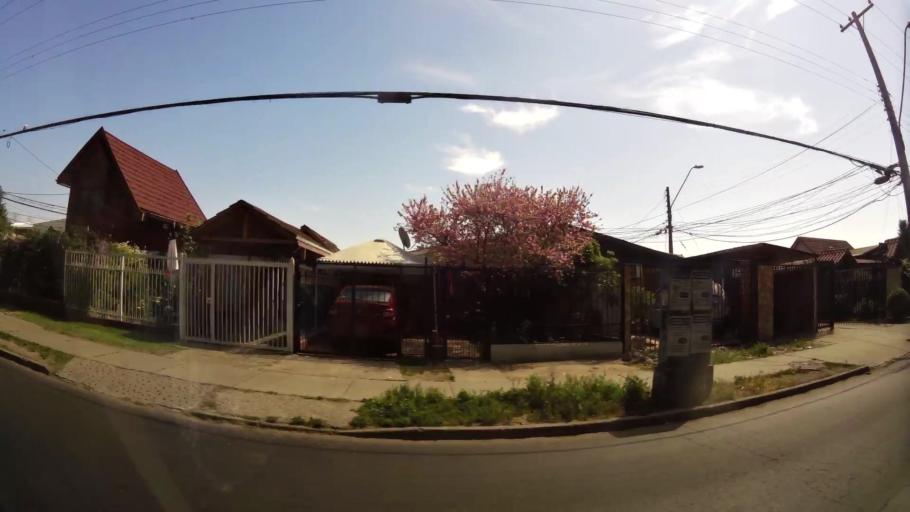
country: CL
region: Santiago Metropolitan
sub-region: Provincia de Santiago
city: Lo Prado
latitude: -33.4748
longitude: -70.7242
